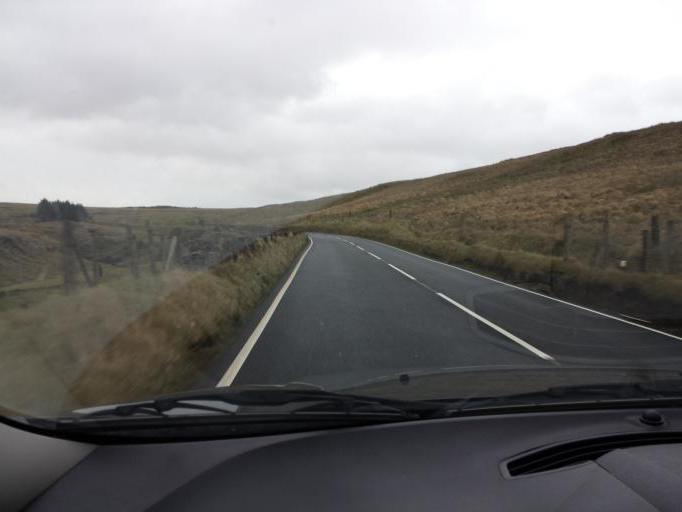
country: GB
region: Northern Ireland
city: Glenariff
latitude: 55.0018
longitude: -6.1629
